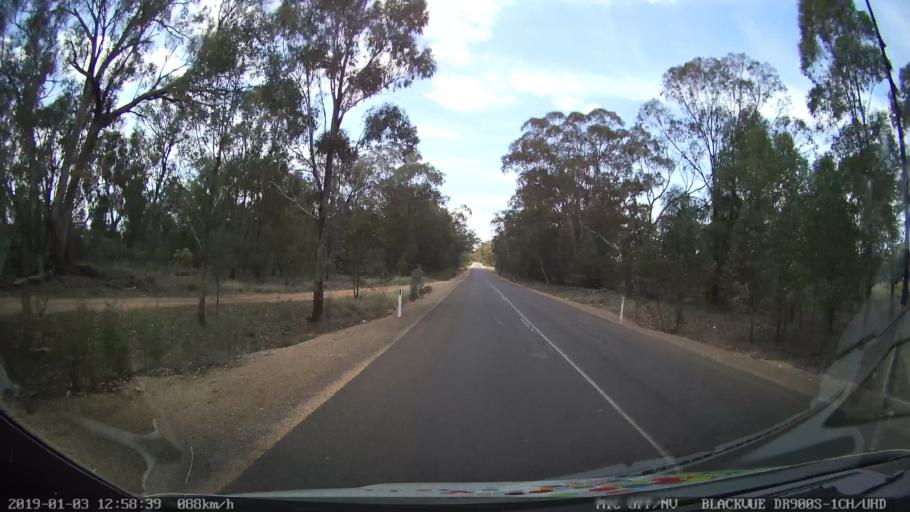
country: AU
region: New South Wales
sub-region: Cabonne
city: Canowindra
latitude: -33.6408
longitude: 148.3779
